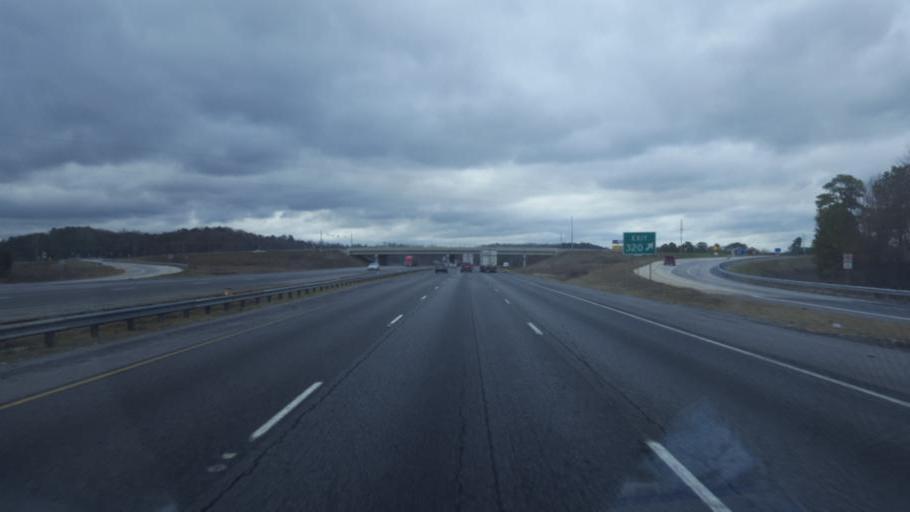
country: US
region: Georgia
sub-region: Gordon County
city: Calhoun
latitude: 34.5746
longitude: -84.9487
